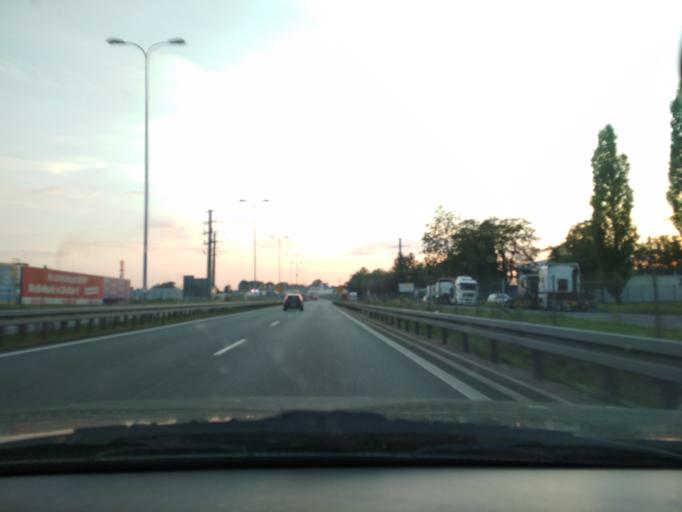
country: PL
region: Silesian Voivodeship
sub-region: Powiat gliwicki
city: Przyszowice
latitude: 50.2684
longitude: 18.7175
